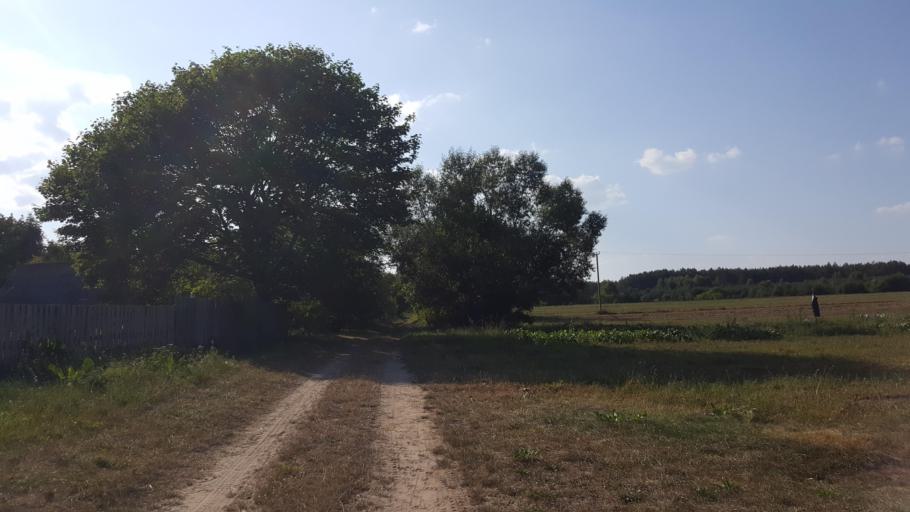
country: BY
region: Brest
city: Kamyanyuki
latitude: 52.5622
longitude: 23.6399
